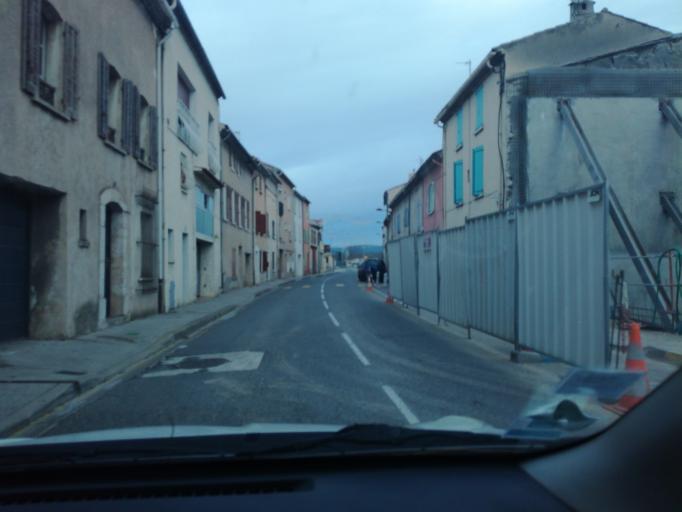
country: FR
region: Provence-Alpes-Cote d'Azur
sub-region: Departement du Var
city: La Crau
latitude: 43.1502
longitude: 6.0736
